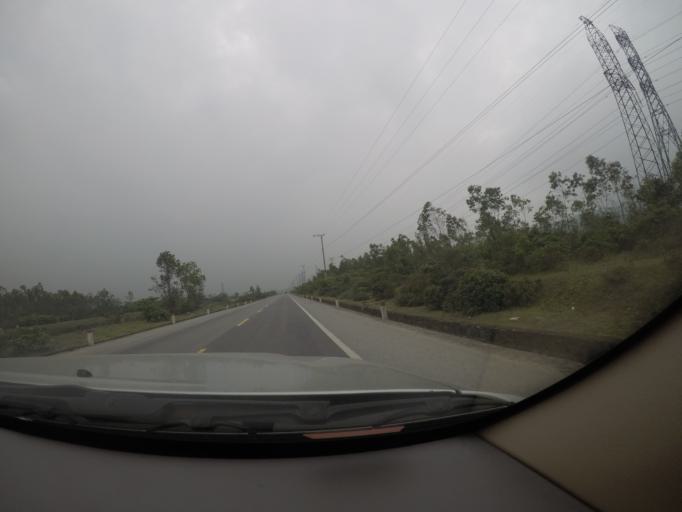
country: VN
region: Ha Tinh
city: Ky Anh
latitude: 18.0070
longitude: 106.4190
